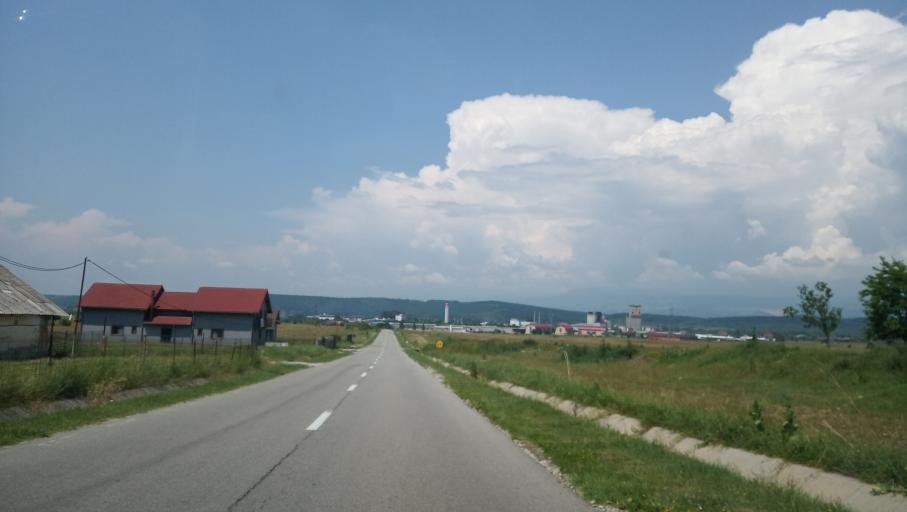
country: RO
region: Gorj
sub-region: Comuna Turcinesti
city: Turcinesti
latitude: 45.0643
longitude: 23.3241
